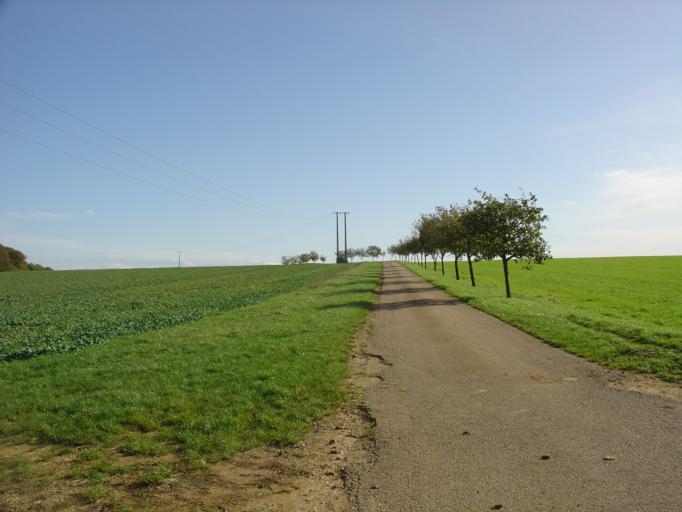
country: FR
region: Lorraine
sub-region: Departement de Meurthe-et-Moselle
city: Villey-Saint-Etienne
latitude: 48.8101
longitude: 5.9527
